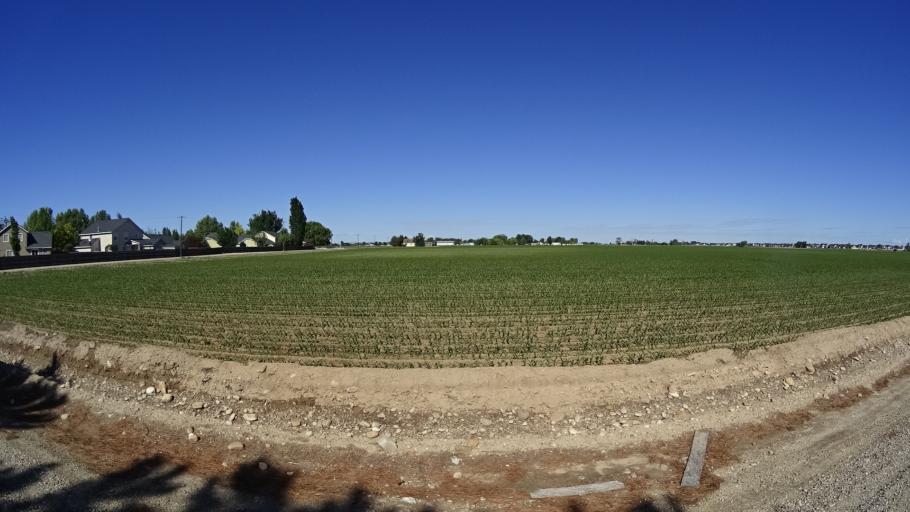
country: US
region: Idaho
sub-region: Ada County
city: Star
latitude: 43.6384
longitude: -116.4536
